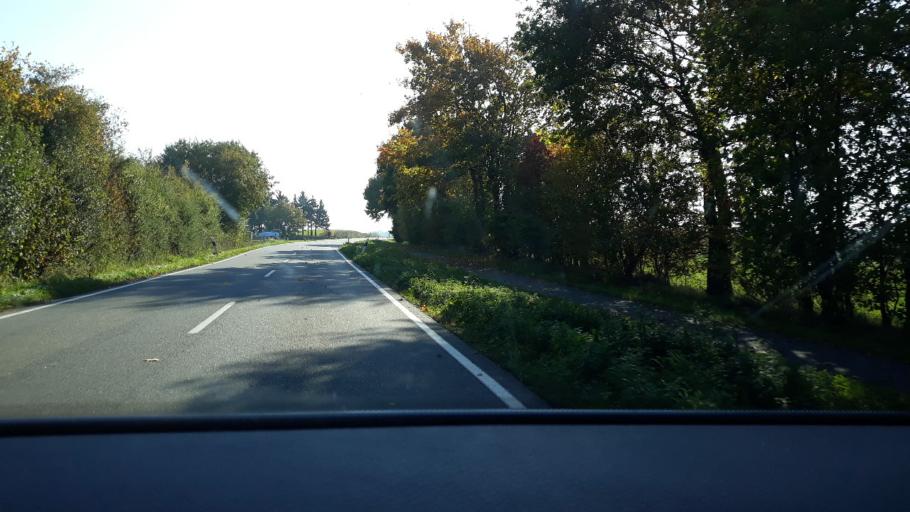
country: DE
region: Schleswig-Holstein
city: Boklund
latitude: 54.5948
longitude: 9.5950
